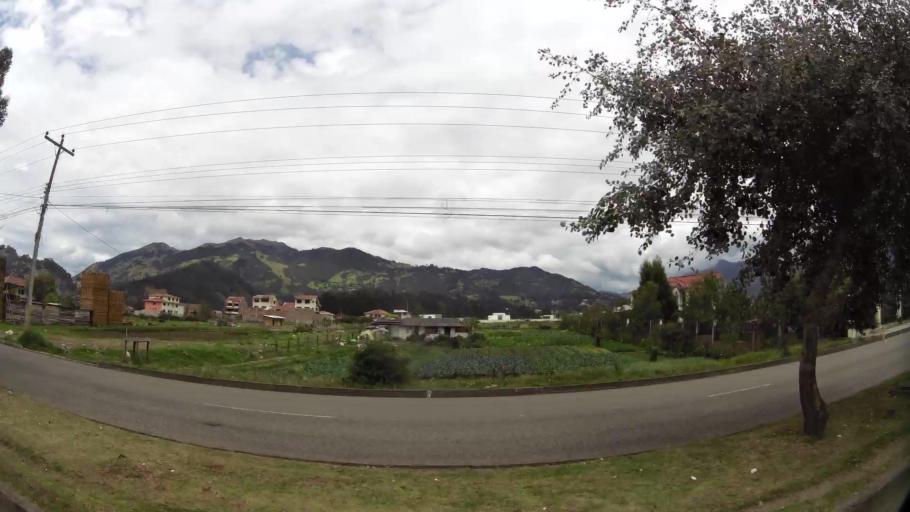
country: EC
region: Azuay
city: Cuenca
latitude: -2.8948
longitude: -79.0546
